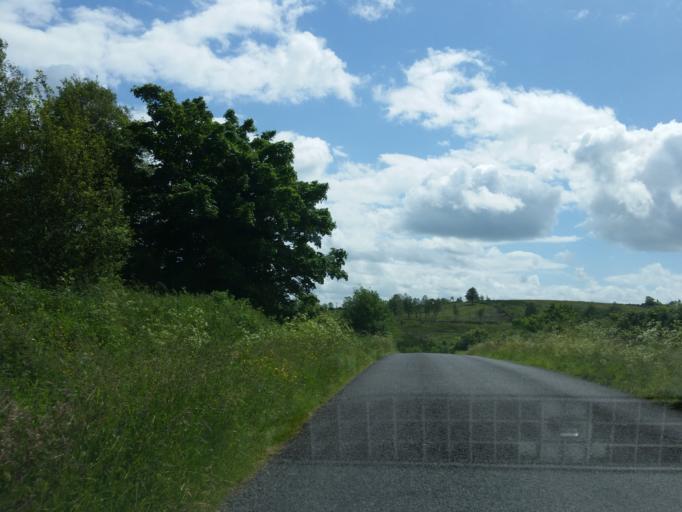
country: GB
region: Northern Ireland
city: Fivemiletown
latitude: 54.3569
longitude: -7.3041
